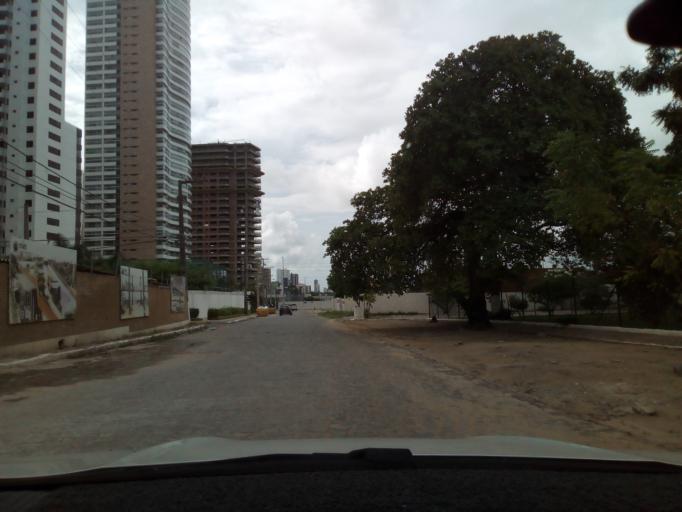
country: BR
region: Paraiba
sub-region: Joao Pessoa
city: Joao Pessoa
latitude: -7.1295
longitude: -34.8268
